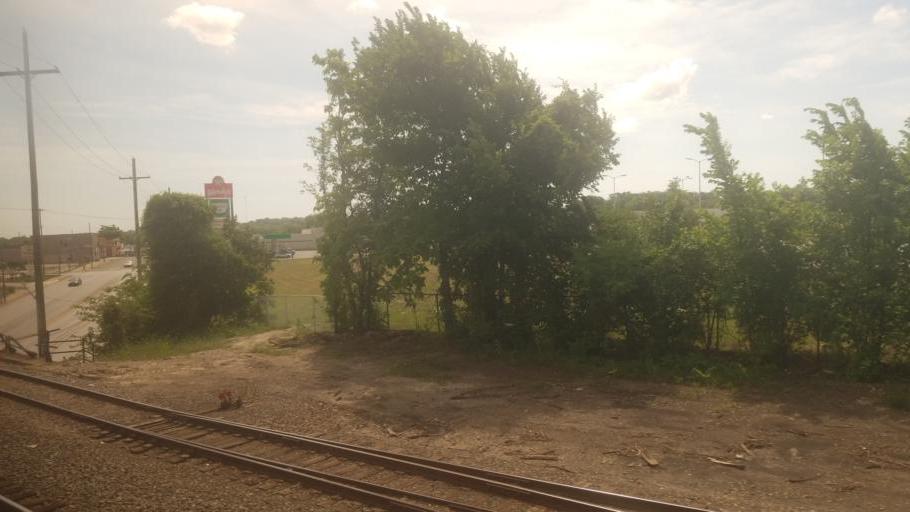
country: US
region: Missouri
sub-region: Jackson County
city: Kansas City
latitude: 39.0940
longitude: -94.5400
